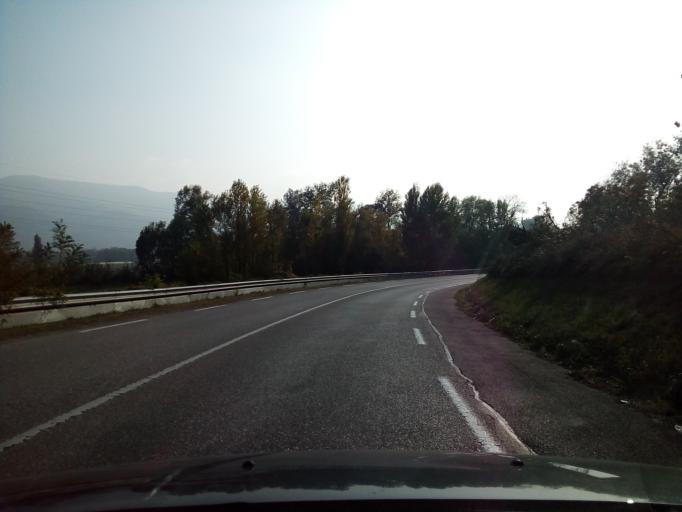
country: FR
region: Rhone-Alpes
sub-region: Departement de l'Isere
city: Saint-Ismier
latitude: 45.2283
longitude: 5.8240
